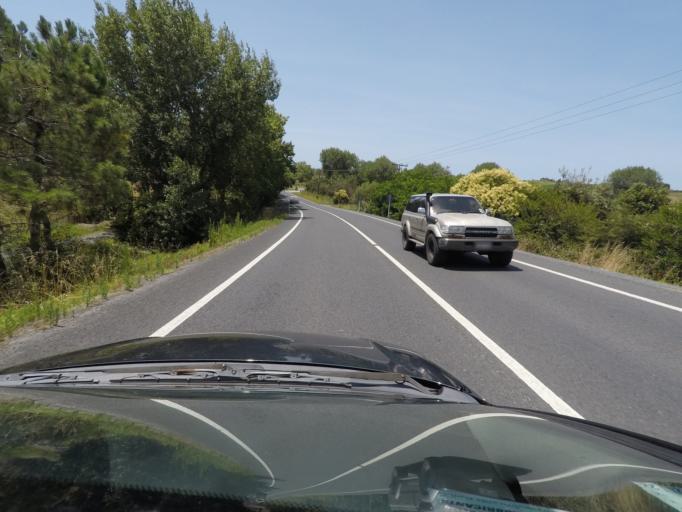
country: NZ
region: Auckland
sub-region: Auckland
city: Warkworth
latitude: -36.3460
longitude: 174.7265
